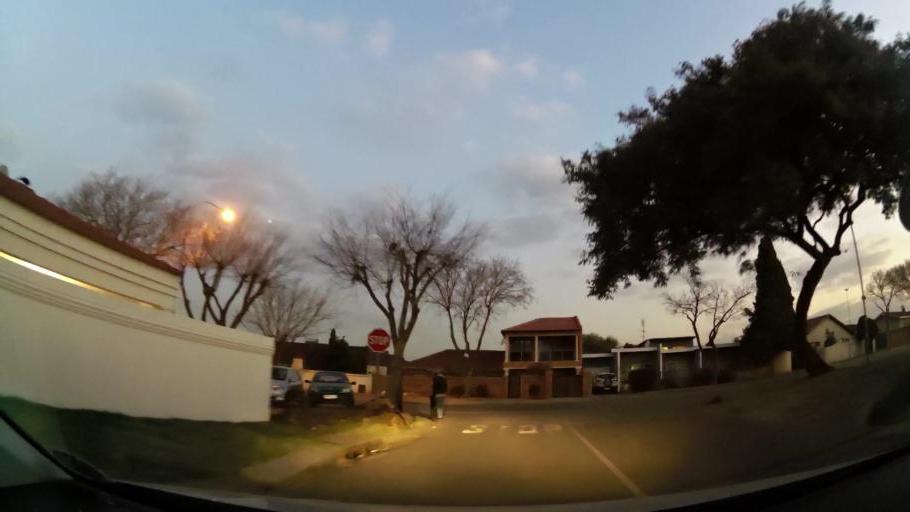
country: ZA
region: Gauteng
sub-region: City of Johannesburg Metropolitan Municipality
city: Soweto
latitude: -26.2719
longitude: 27.9057
